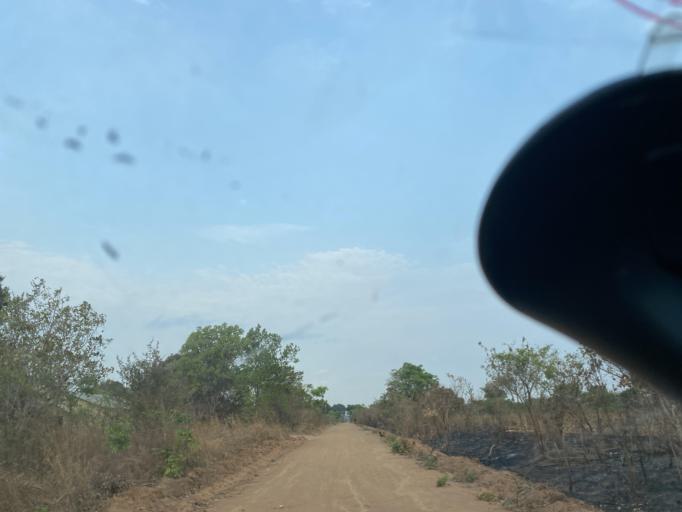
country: ZM
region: Lusaka
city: Chongwe
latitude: -15.2024
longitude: 28.5226
